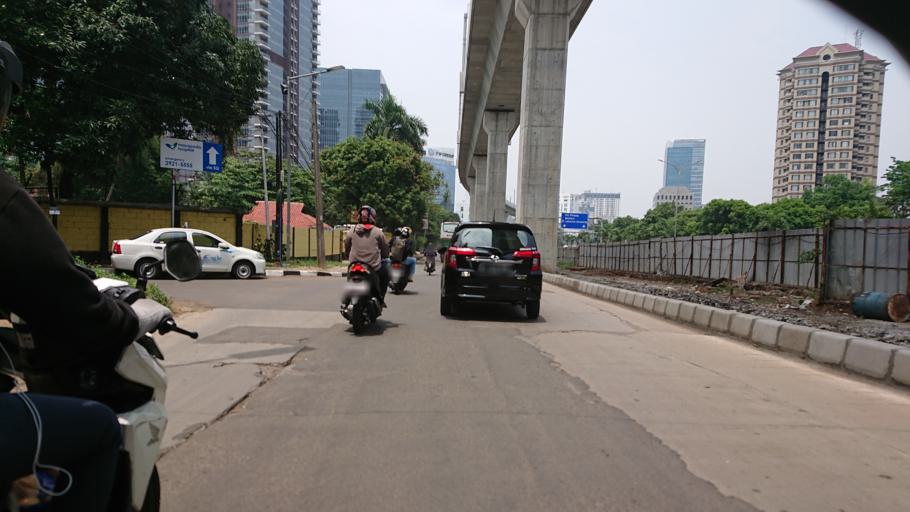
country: ID
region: Banten
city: South Tangerang
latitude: -6.2925
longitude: 106.7884
